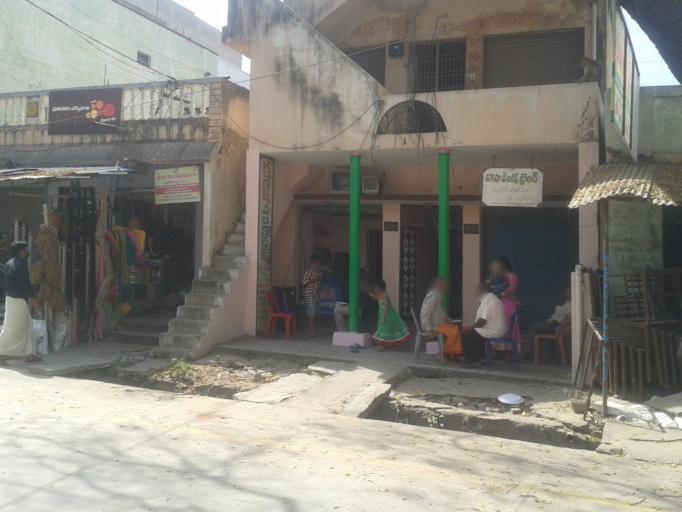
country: IN
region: Andhra Pradesh
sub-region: Chittoor
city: Narasingapuram
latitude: 13.5857
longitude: 79.3151
